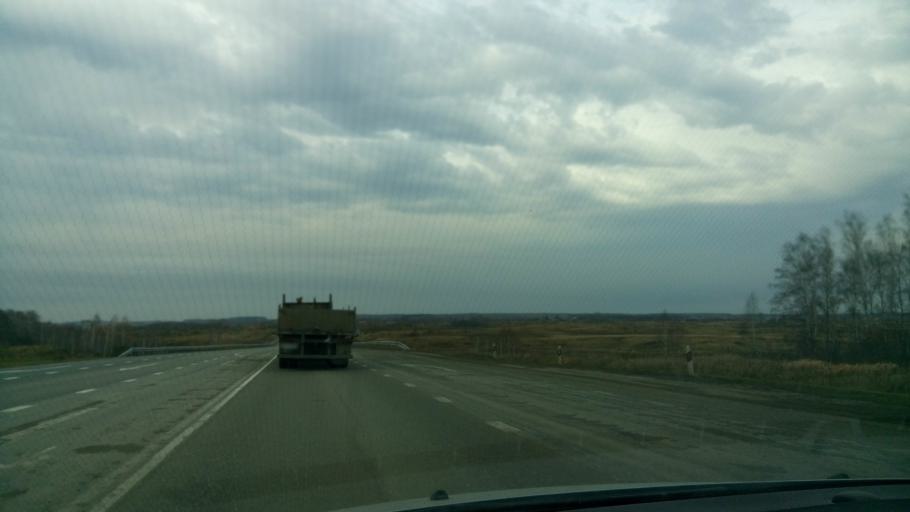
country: RU
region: Sverdlovsk
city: Kamyshlov
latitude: 56.8709
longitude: 62.7415
